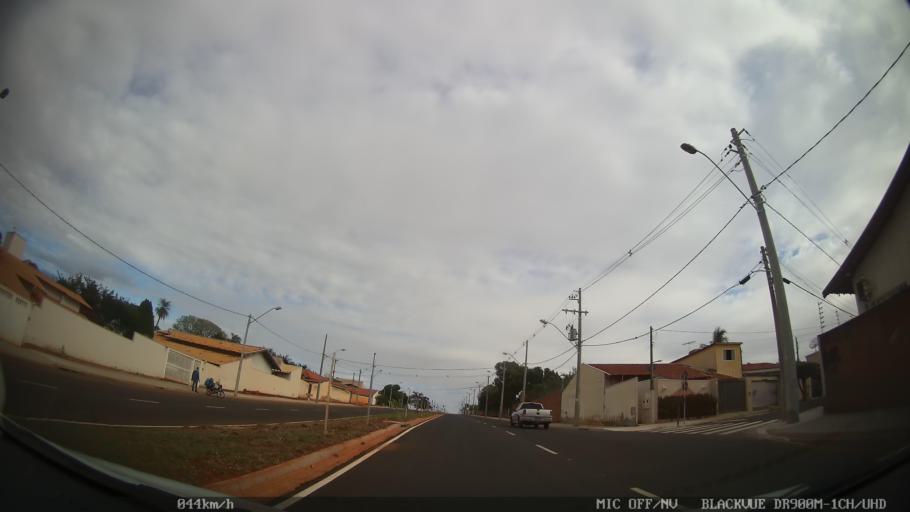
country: BR
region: Sao Paulo
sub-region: Sao Jose Do Rio Preto
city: Sao Jose do Rio Preto
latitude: -20.8293
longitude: -49.4107
